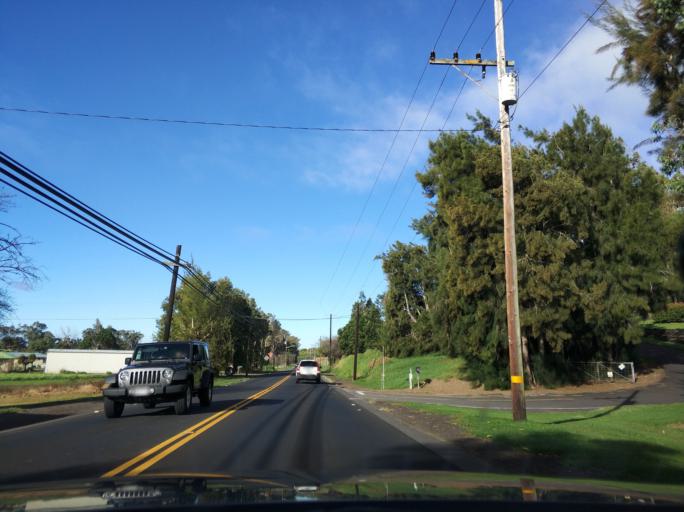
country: US
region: Hawaii
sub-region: Hawaii County
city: Waimea
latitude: 20.0285
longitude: -155.6465
